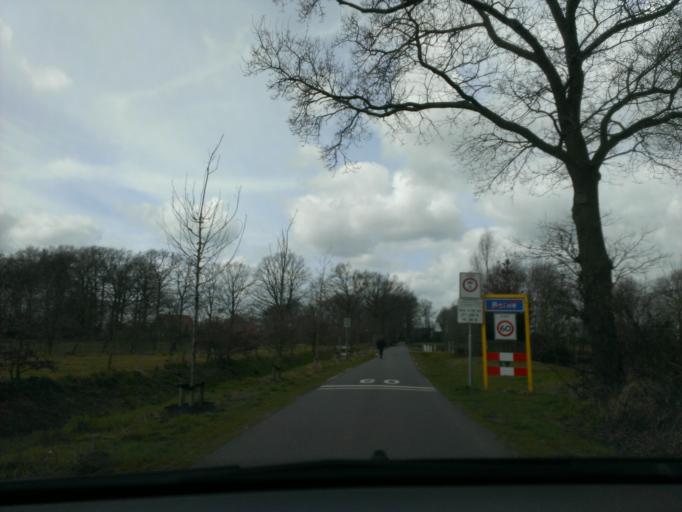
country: NL
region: Overijssel
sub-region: Gemeente Borne
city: Borne
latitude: 52.3062
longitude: 6.7347
